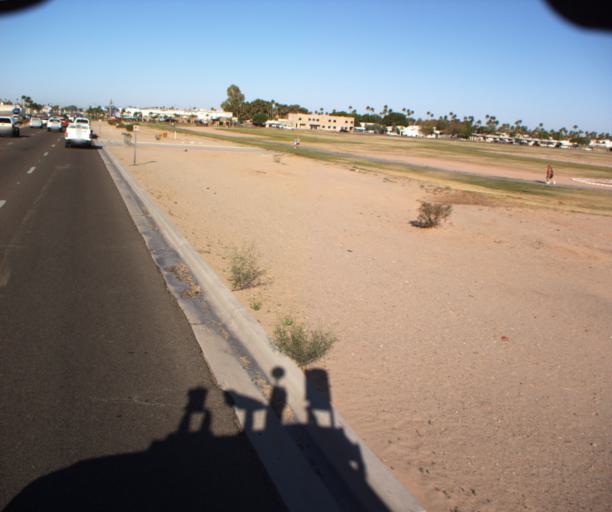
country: US
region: Arizona
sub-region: Yuma County
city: Yuma
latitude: 32.6695
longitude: -114.6021
